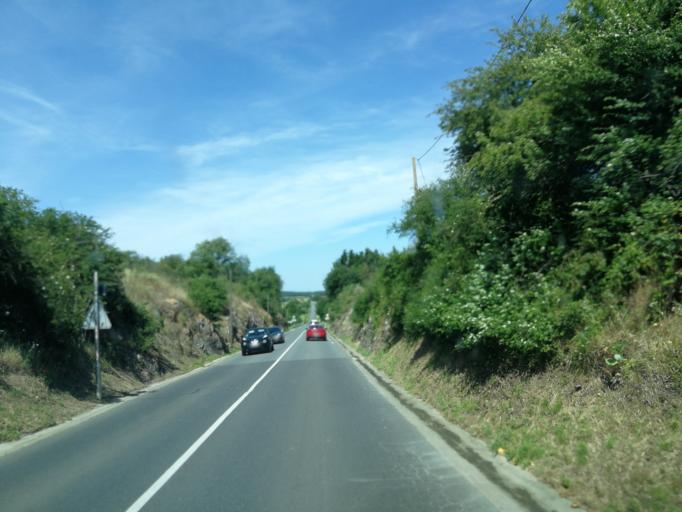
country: FR
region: Poitou-Charentes
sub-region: Departement des Deux-Sevres
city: Saint-Varent
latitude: 46.9162
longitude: -0.2702
